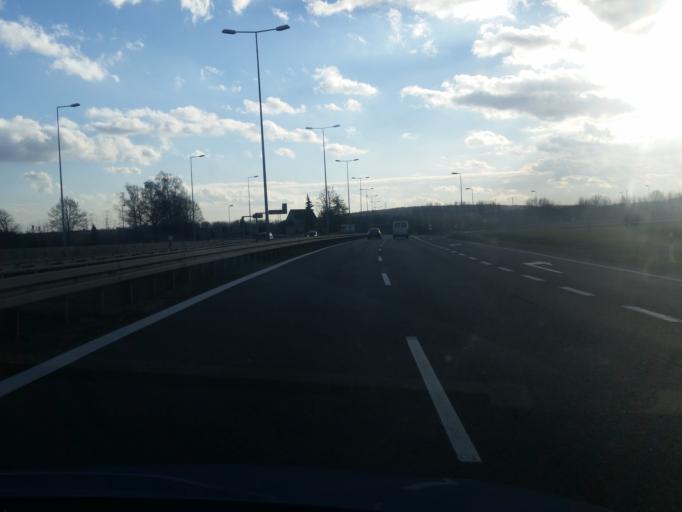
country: PL
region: Silesian Voivodeship
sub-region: Powiat bedzinski
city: Siewierz
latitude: 50.4591
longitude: 19.2315
